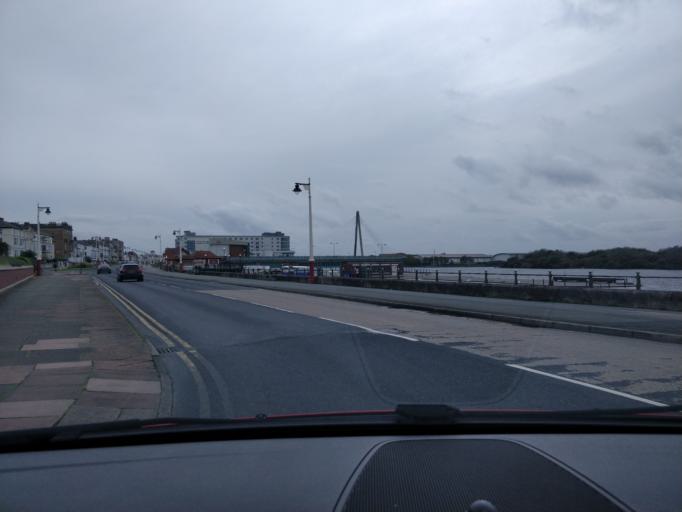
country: GB
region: England
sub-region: Sefton
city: Southport
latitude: 53.6546
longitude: -3.0030
